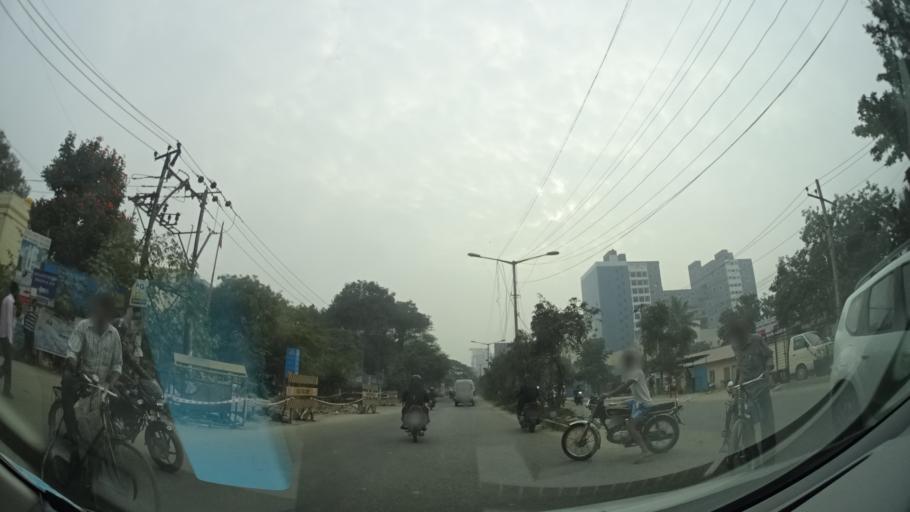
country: IN
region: Karnataka
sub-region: Bangalore Urban
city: Bangalore
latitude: 12.9951
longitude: 77.6979
